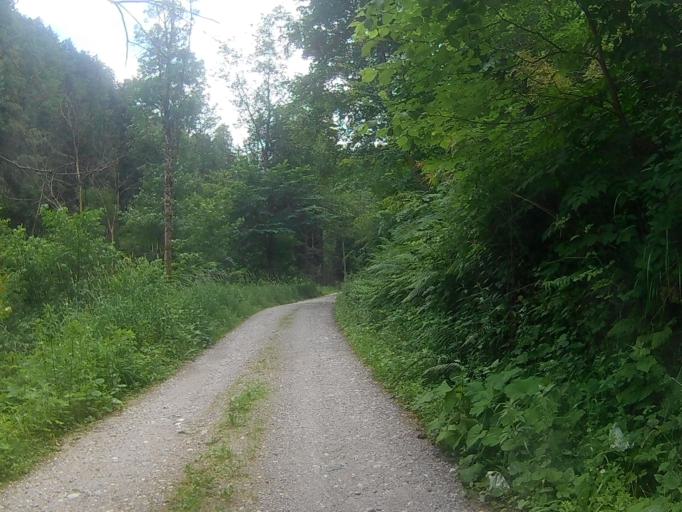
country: SI
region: Selnica ob Dravi
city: Selnica ob Dravi
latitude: 46.5183
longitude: 15.4553
